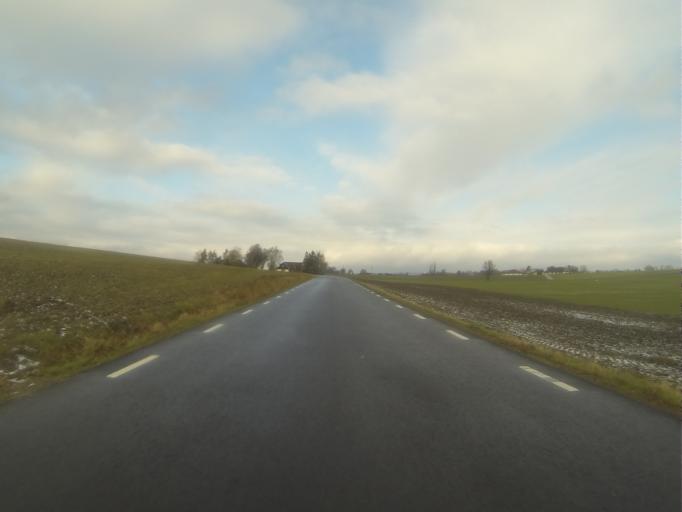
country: SE
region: Skane
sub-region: Svedala Kommun
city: Klagerup
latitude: 55.6178
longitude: 13.3089
